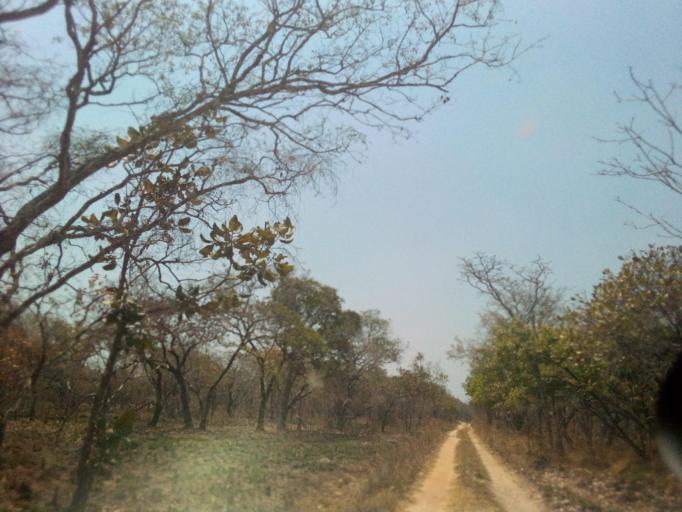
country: ZM
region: Copperbelt
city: Kataba
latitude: -12.2426
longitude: 30.4000
